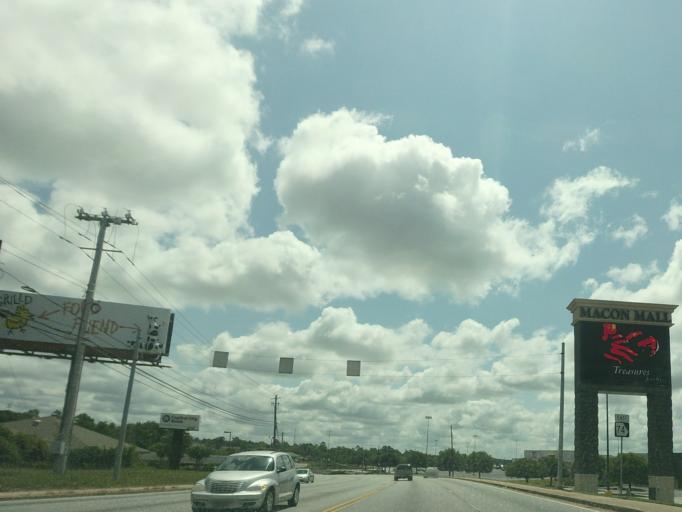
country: US
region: Georgia
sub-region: Bibb County
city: Macon
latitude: 32.8209
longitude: -83.6953
